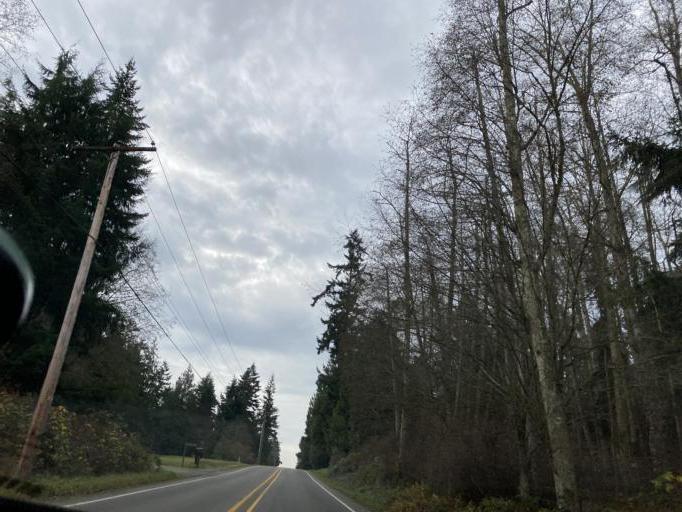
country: US
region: Washington
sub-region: Island County
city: Freeland
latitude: 47.9996
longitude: -122.5370
